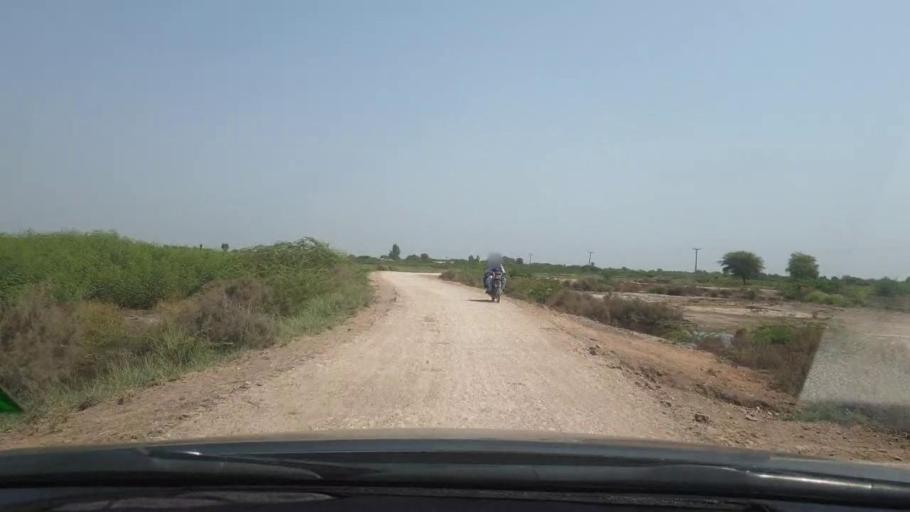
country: PK
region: Sindh
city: Tando Bago
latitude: 24.7830
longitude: 69.1812
